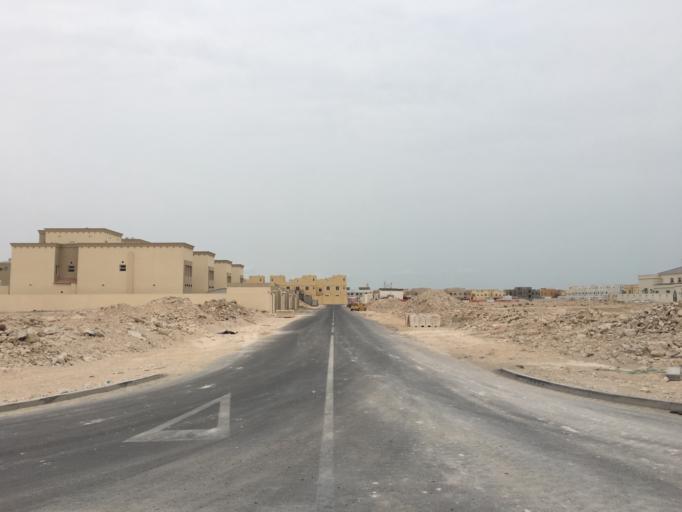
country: QA
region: Baladiyat Umm Salal
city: Umm Salal Muhammad
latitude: 25.3907
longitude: 51.4371
